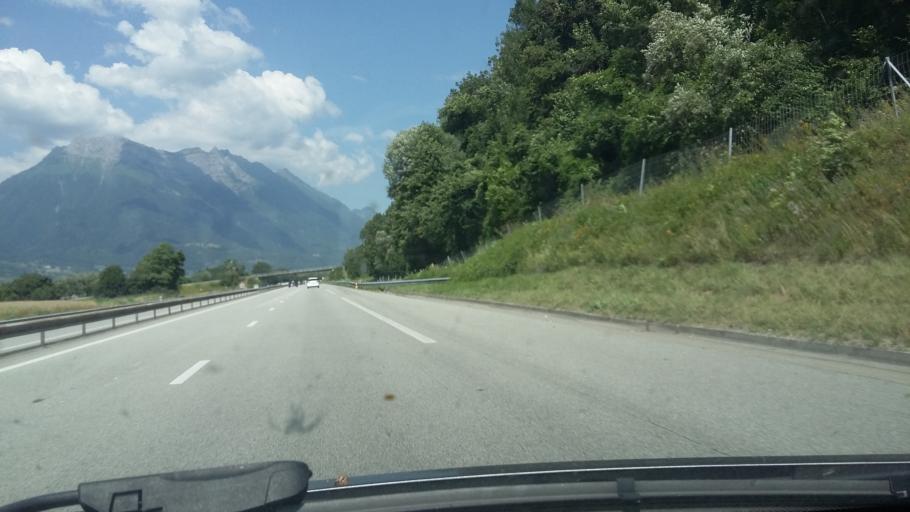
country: FR
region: Rhone-Alpes
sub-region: Departement de la Savoie
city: Cruet
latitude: 45.5252
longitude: 6.1163
